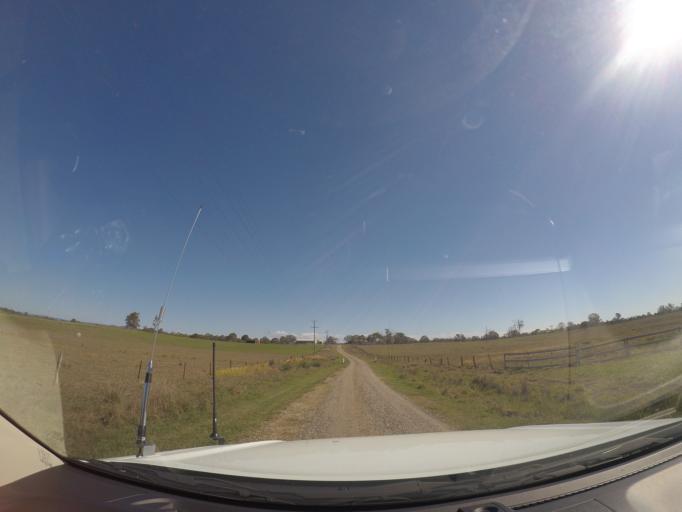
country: AU
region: Queensland
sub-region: Logan
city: North Maclean
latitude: -27.7670
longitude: 153.0471
